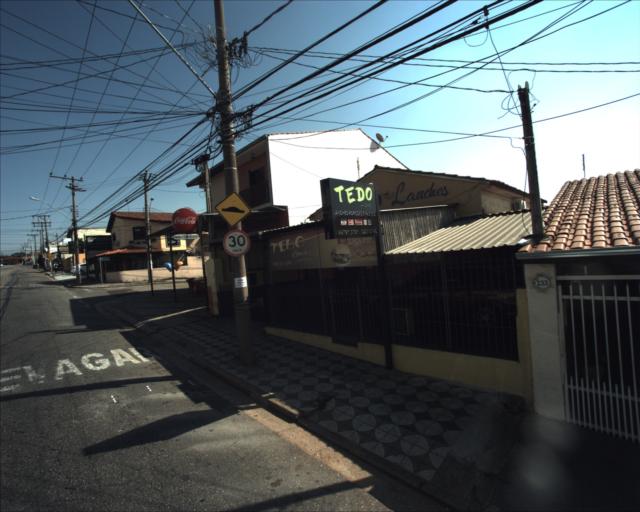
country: BR
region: Sao Paulo
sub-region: Sorocaba
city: Sorocaba
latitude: -23.4829
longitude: -47.4520
